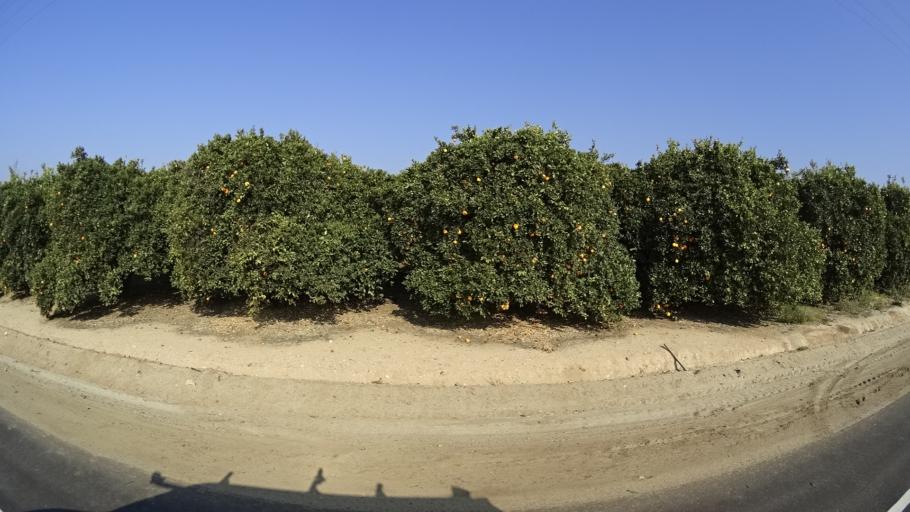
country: US
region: California
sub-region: Kern County
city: Lamont
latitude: 35.3618
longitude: -118.8822
